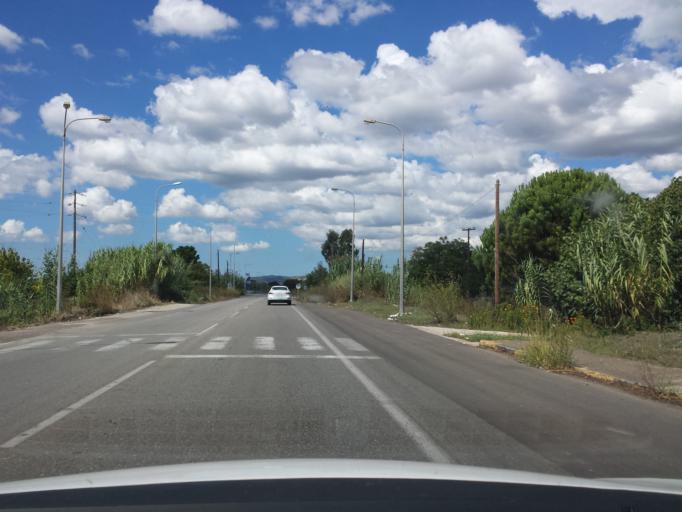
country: GR
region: West Greece
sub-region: Nomos Ileias
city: Pyrgos
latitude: 37.6572
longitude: 21.4650
